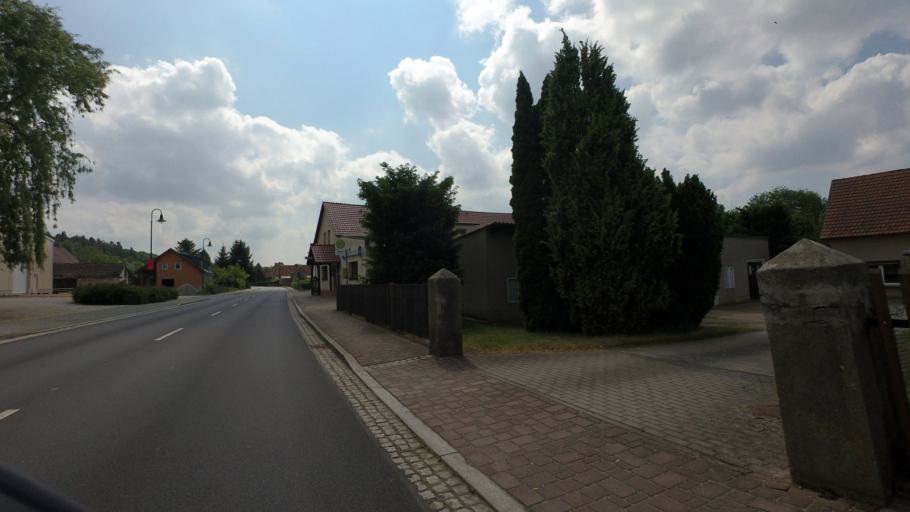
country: DE
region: Saxony
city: Rietschen
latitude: 51.3591
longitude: 14.8034
